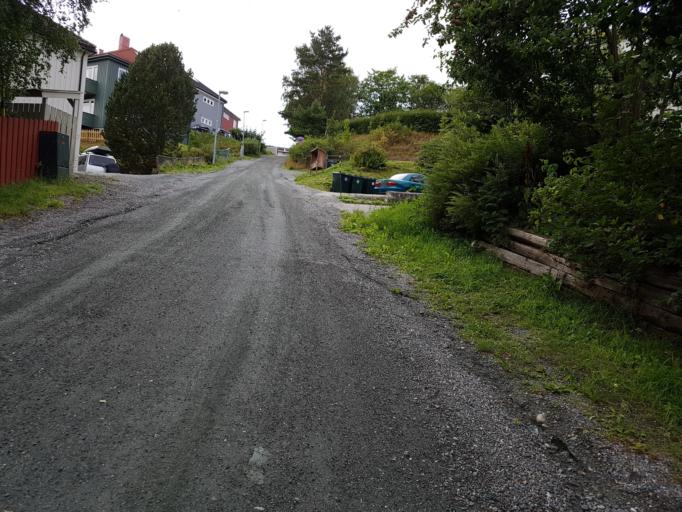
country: NO
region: Sor-Trondelag
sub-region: Trondheim
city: Trondheim
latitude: 63.4458
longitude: 10.4315
